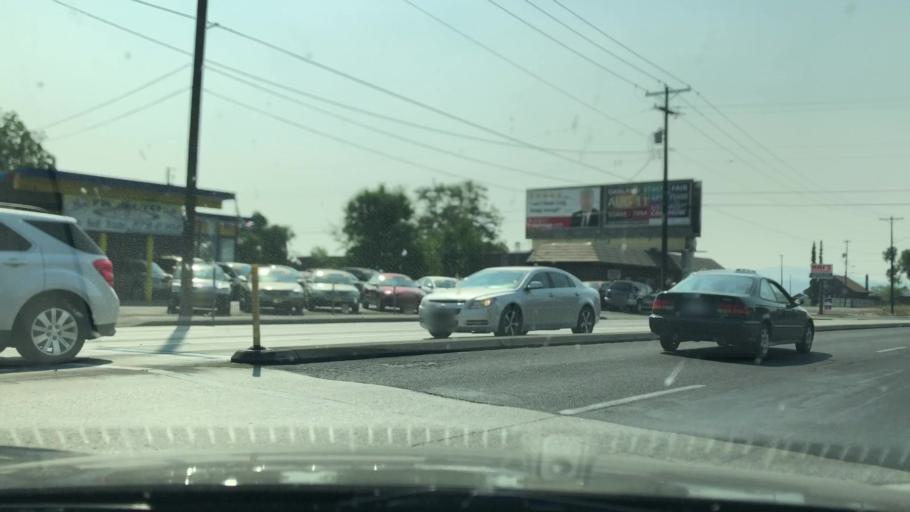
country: US
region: Washington
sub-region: Spokane County
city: Spokane
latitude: 47.6861
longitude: -117.3652
